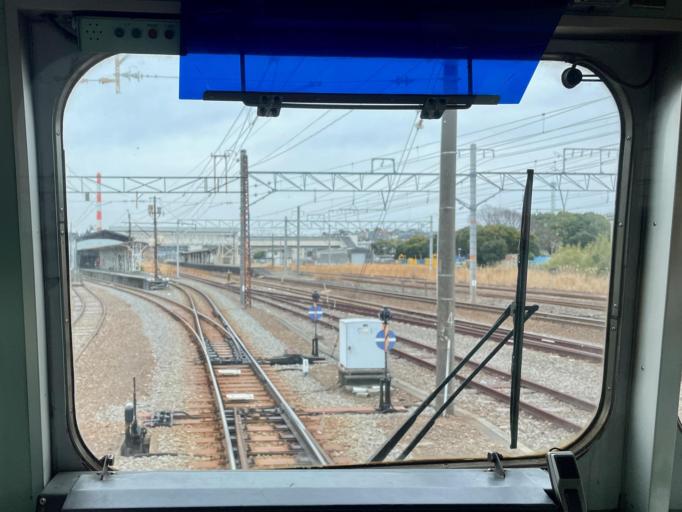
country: JP
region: Shizuoka
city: Fuji
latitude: 35.1446
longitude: 138.7004
